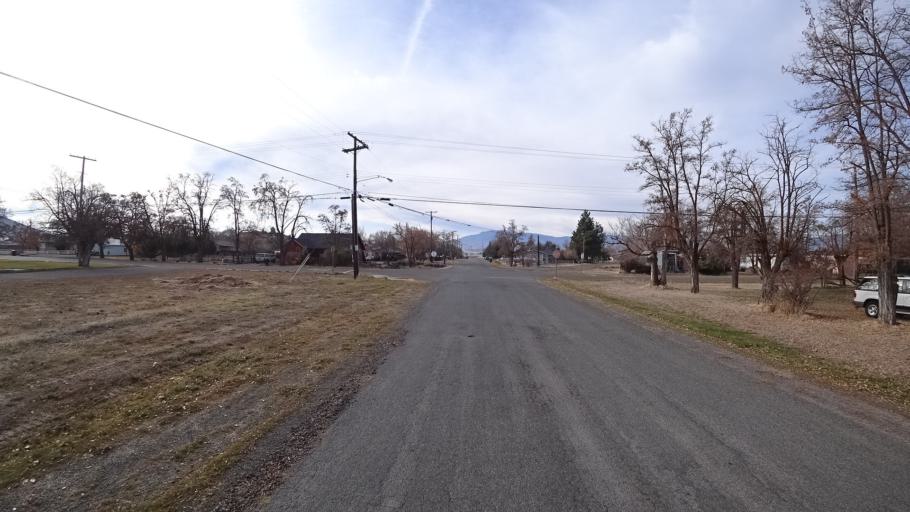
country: US
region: California
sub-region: Siskiyou County
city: Montague
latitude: 41.7277
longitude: -122.5329
